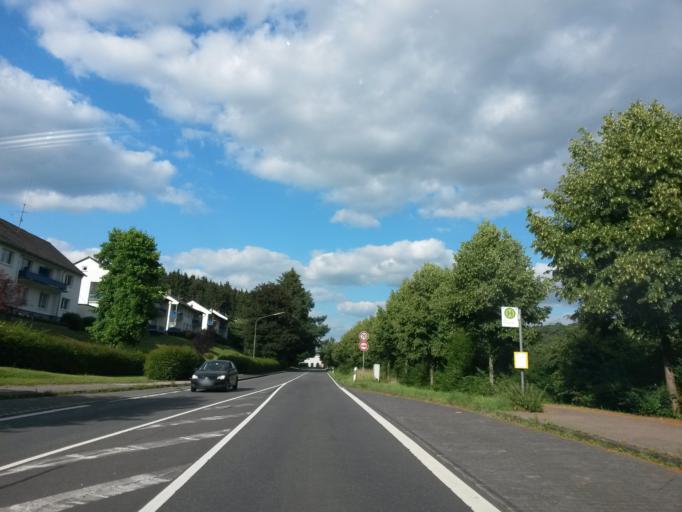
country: DE
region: North Rhine-Westphalia
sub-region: Regierungsbezirk Koln
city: Ruppichteroth
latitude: 50.8390
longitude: 7.4729
